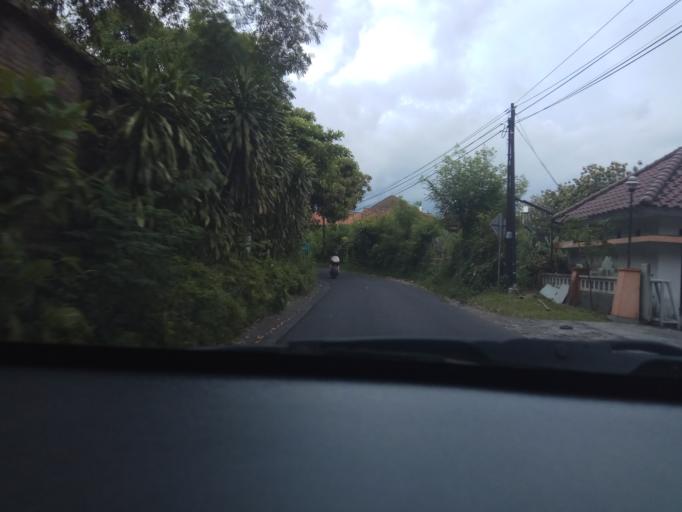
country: ID
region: Daerah Istimewa Yogyakarta
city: Depok
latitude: -7.7631
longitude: 110.3943
